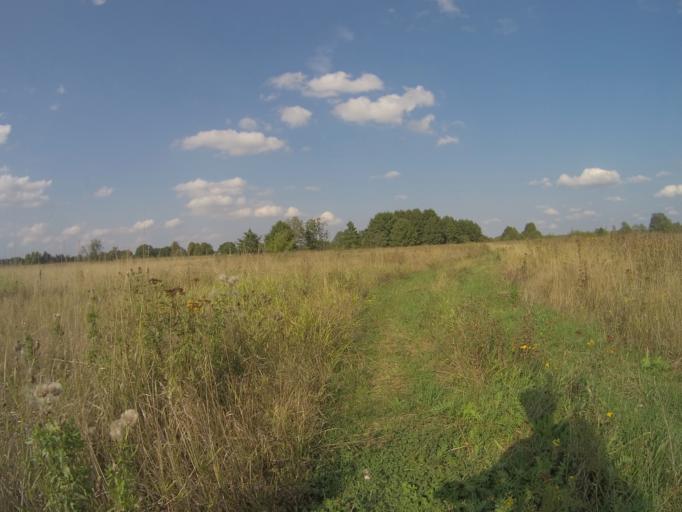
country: RU
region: Vladimir
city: Raduzhnyy
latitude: 56.0387
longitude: 40.3053
